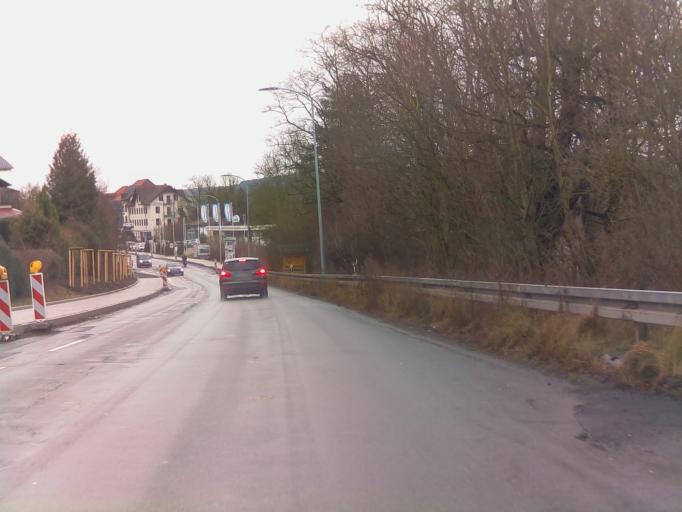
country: DE
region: Hesse
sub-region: Regierungsbezirk Kassel
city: Eichenzell
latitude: 50.5206
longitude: 9.6818
